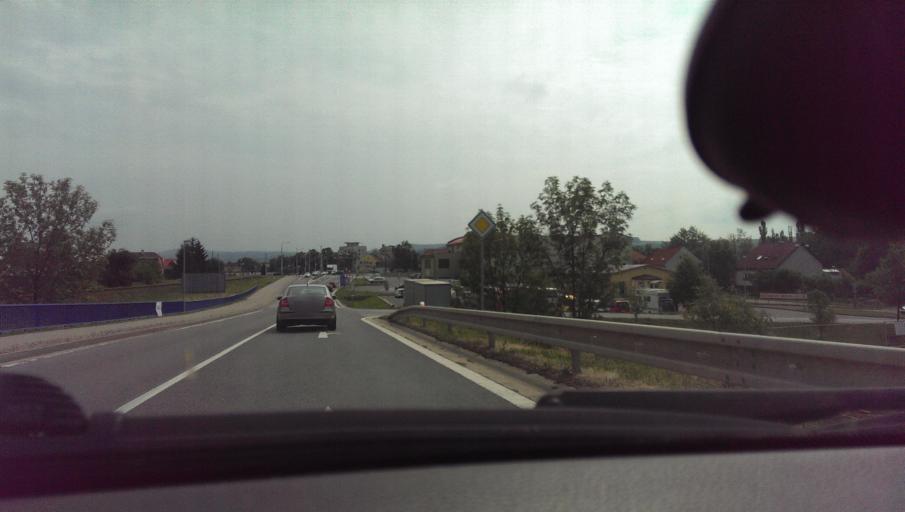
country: CZ
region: Zlin
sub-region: Okres Zlin
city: Otrokovice
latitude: 49.1991
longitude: 17.5339
